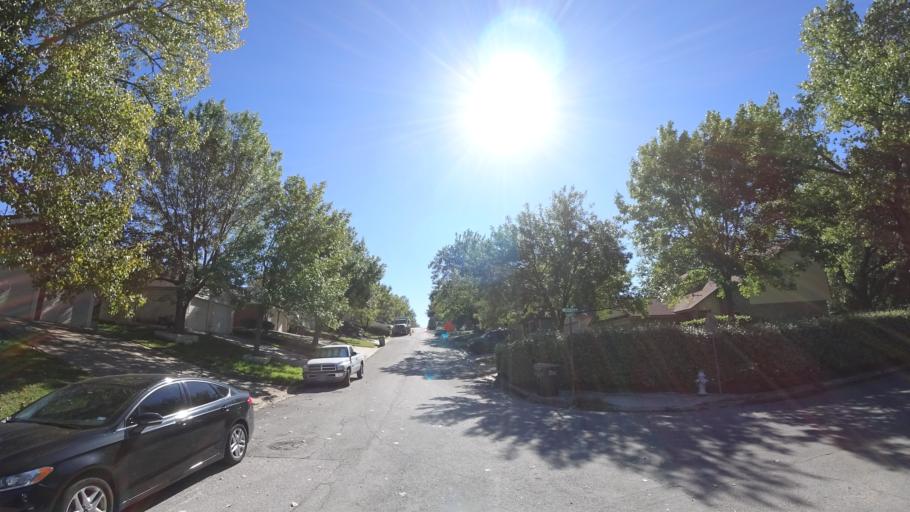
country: US
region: Texas
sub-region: Travis County
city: Manor
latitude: 30.3346
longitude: -97.6486
